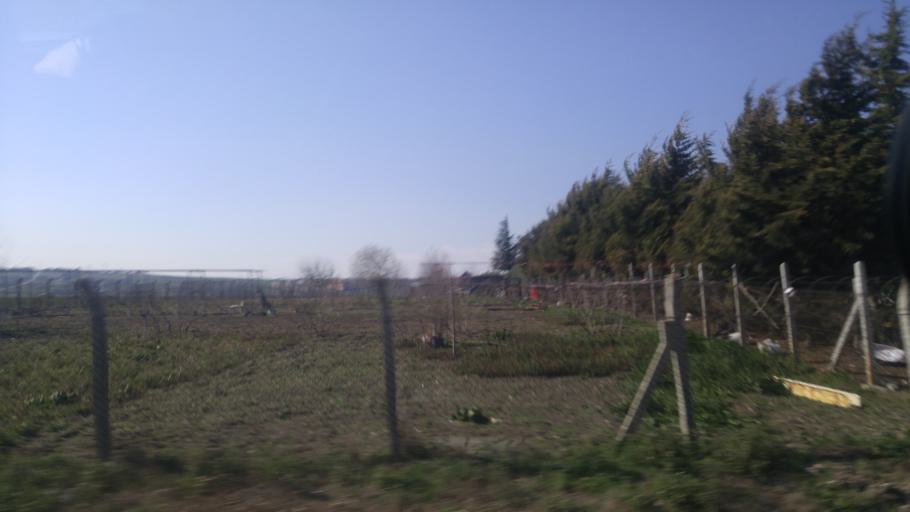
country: TR
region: Istanbul
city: Canta
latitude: 41.0948
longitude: 28.1097
